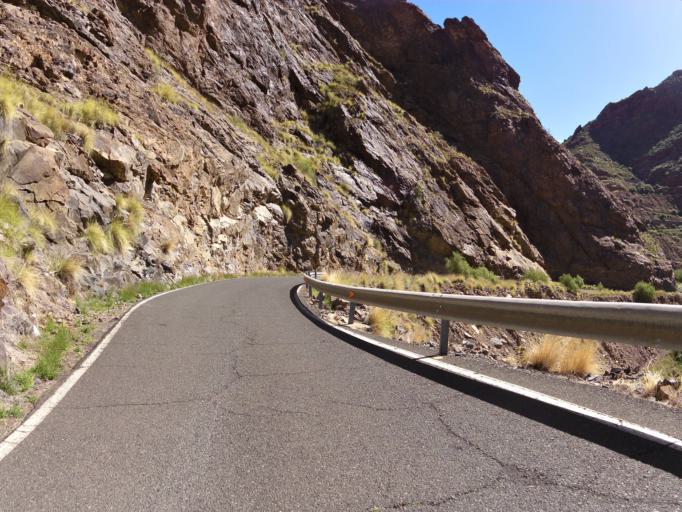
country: ES
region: Canary Islands
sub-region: Provincia de Las Palmas
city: Artenara
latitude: 27.9932
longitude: -15.7088
